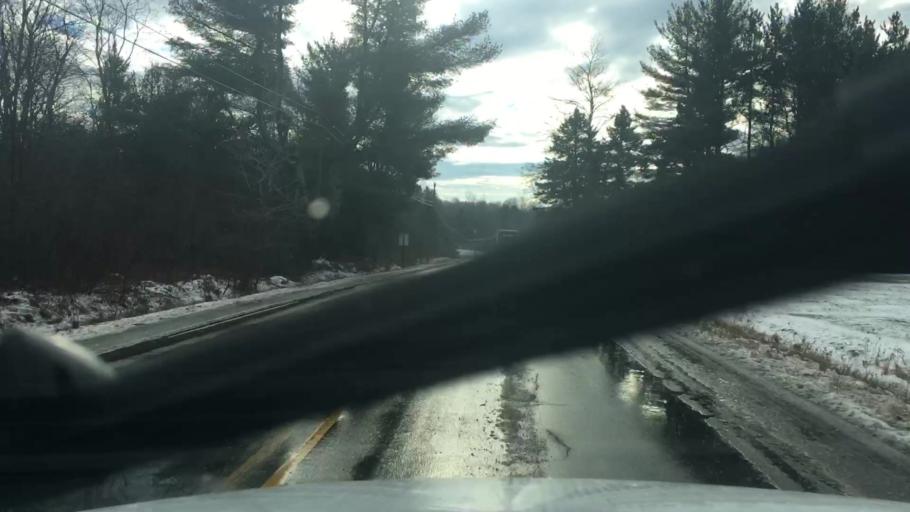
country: US
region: Maine
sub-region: Penobscot County
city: Brewer
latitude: 44.7434
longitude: -68.7657
